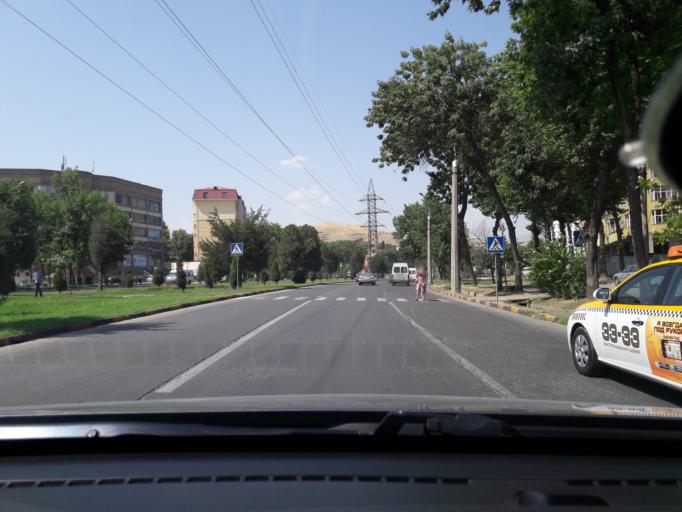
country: TJ
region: Dushanbe
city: Dushanbe
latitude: 38.5884
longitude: 68.7412
